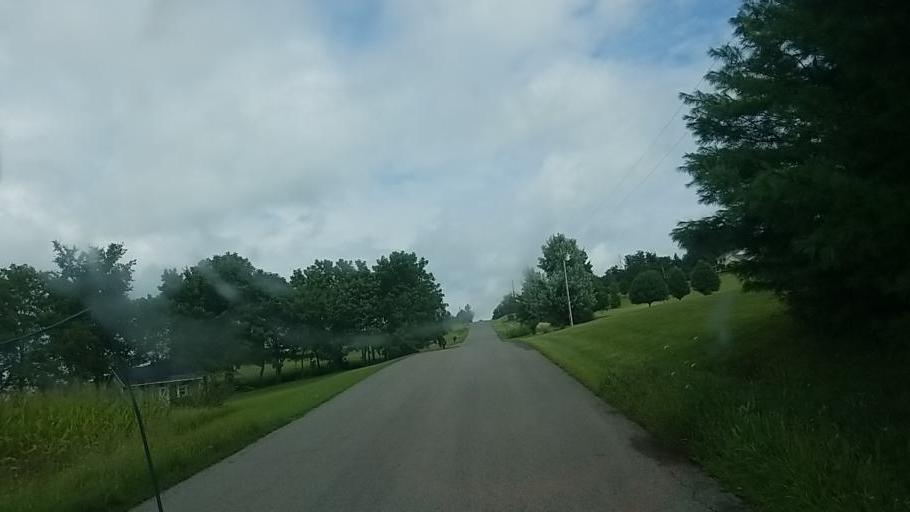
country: US
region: Ohio
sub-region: Champaign County
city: North Lewisburg
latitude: 40.2585
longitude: -83.6296
